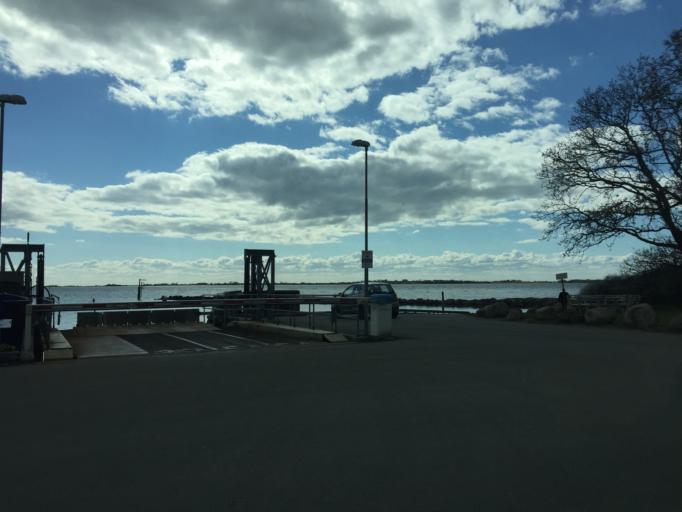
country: DK
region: Zealand
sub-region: Slagelse Kommune
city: Skaelskor
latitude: 55.2129
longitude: 11.2446
